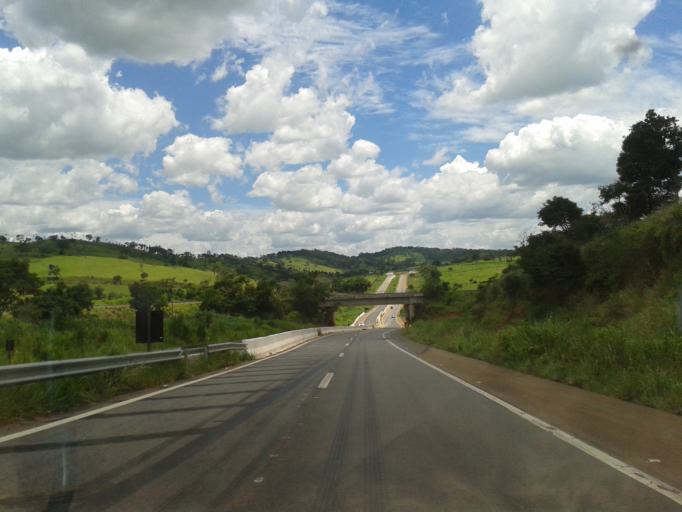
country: BR
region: Goias
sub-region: Neropolis
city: Neropolis
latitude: -16.2837
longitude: -49.2895
